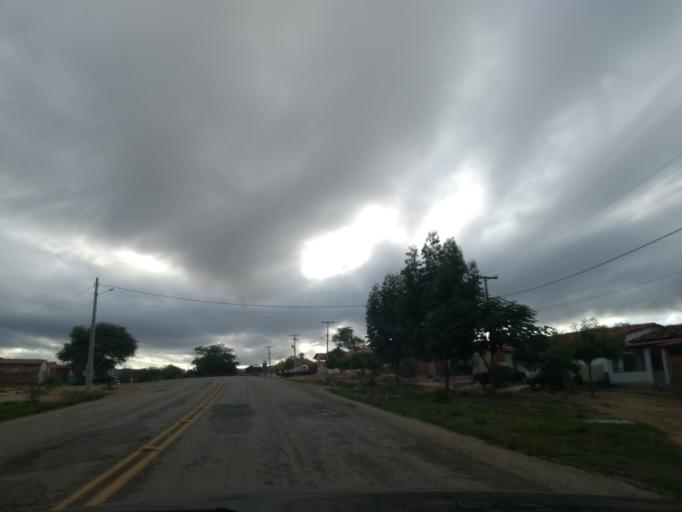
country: BR
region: Bahia
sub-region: Ituacu
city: Ituacu
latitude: -13.7614
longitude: -41.0333
